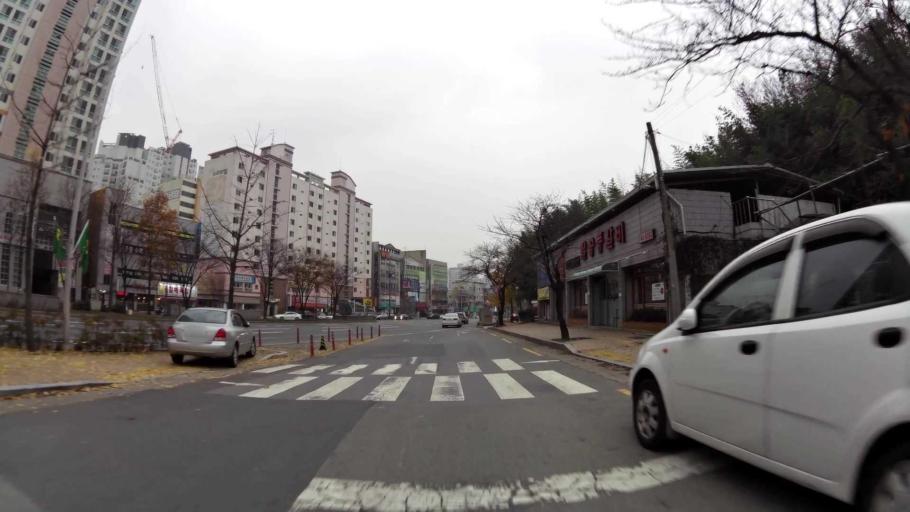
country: KR
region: Daegu
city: Daegu
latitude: 35.8548
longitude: 128.6554
